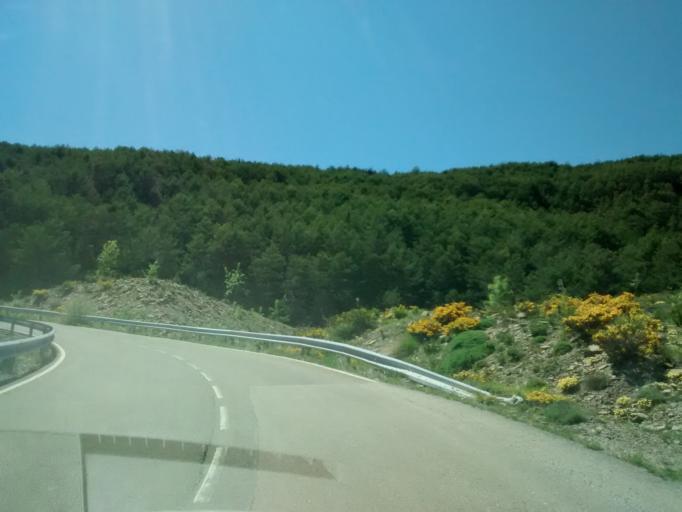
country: ES
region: Aragon
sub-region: Provincia de Huesca
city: Borau
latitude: 42.6545
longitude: -0.5728
